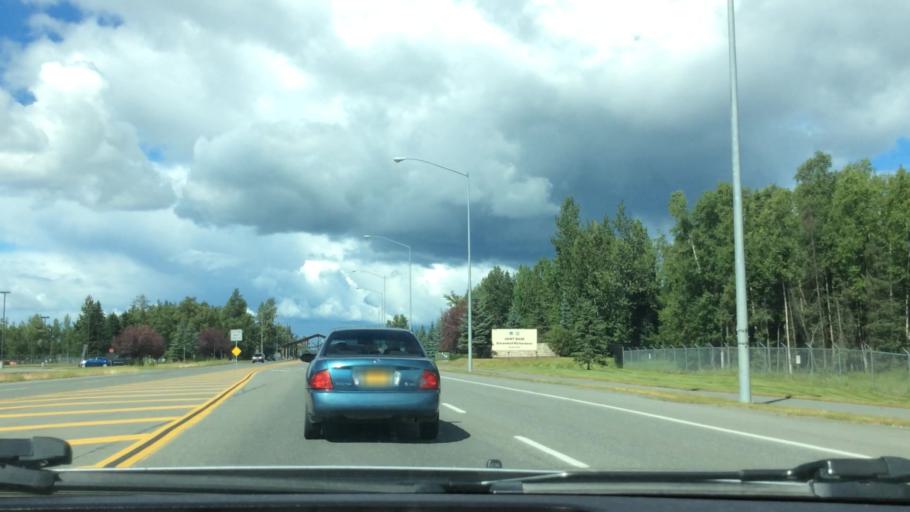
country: US
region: Alaska
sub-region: Anchorage Municipality
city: Anchorage
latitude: 61.2274
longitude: -149.7784
